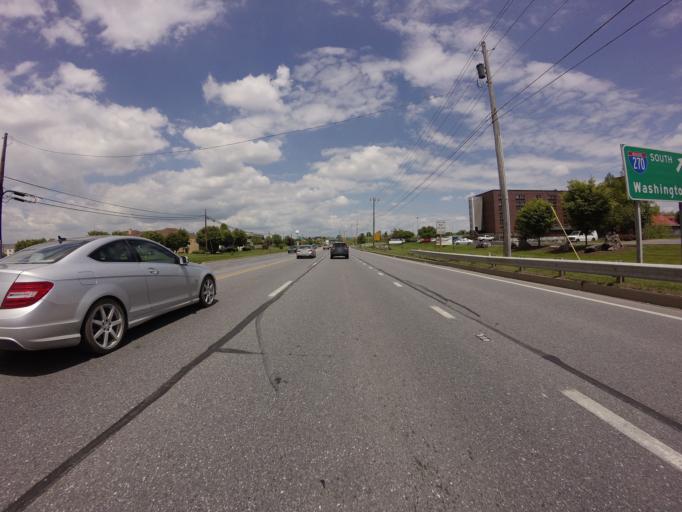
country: US
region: Maryland
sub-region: Frederick County
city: Ballenger Creek
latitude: 39.3777
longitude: -77.4093
